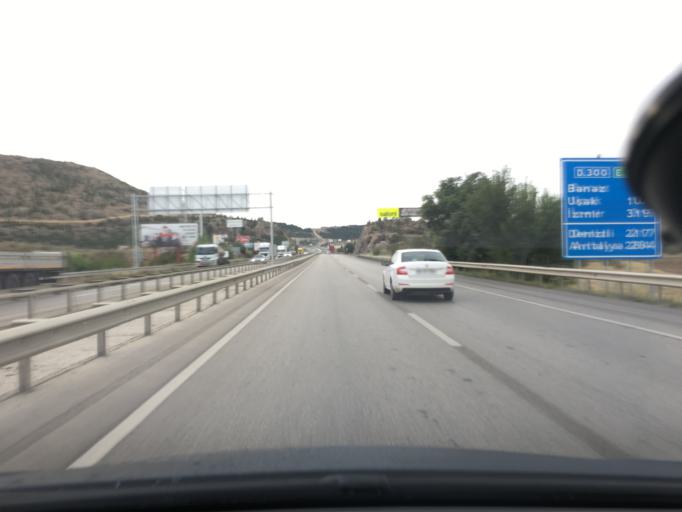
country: TR
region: Afyonkarahisar
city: Afyonkarahisar
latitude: 38.7924
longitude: 30.4499
